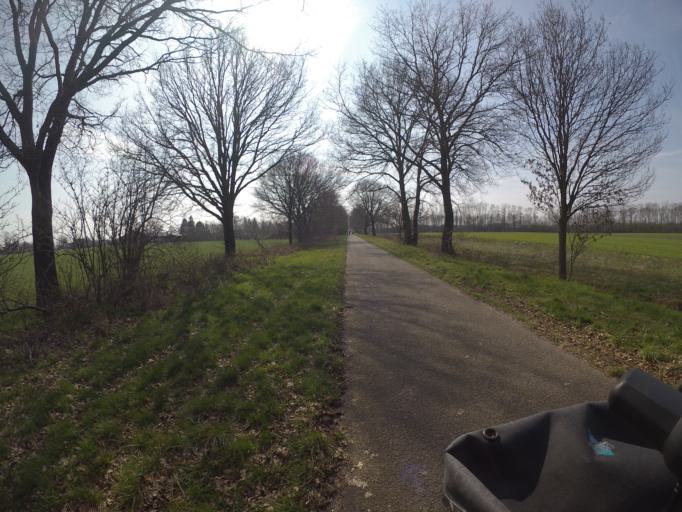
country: NL
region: North Brabant
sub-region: Gemeente Baarle-Nassau
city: Baarle-Nassau
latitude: 51.4913
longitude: 4.9751
